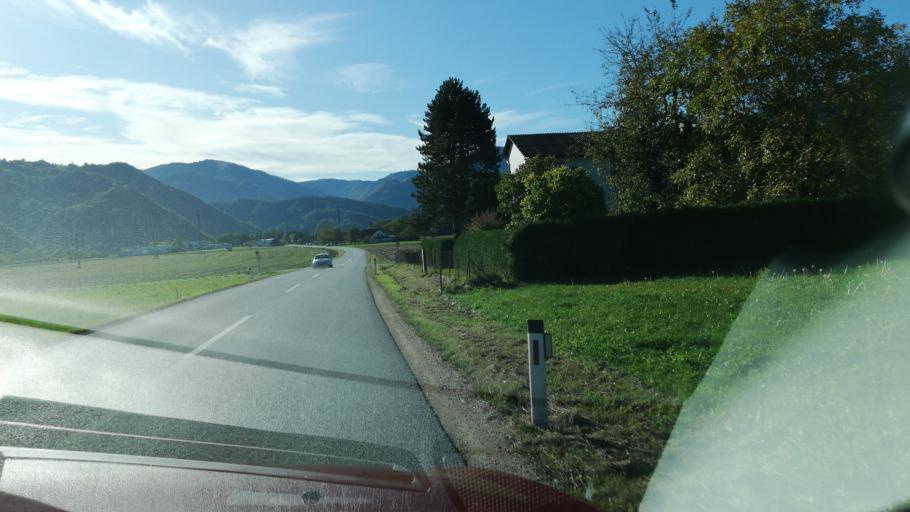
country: AT
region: Upper Austria
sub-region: Politischer Bezirk Steyr-Land
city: Ternberg
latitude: 47.9630
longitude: 14.3473
